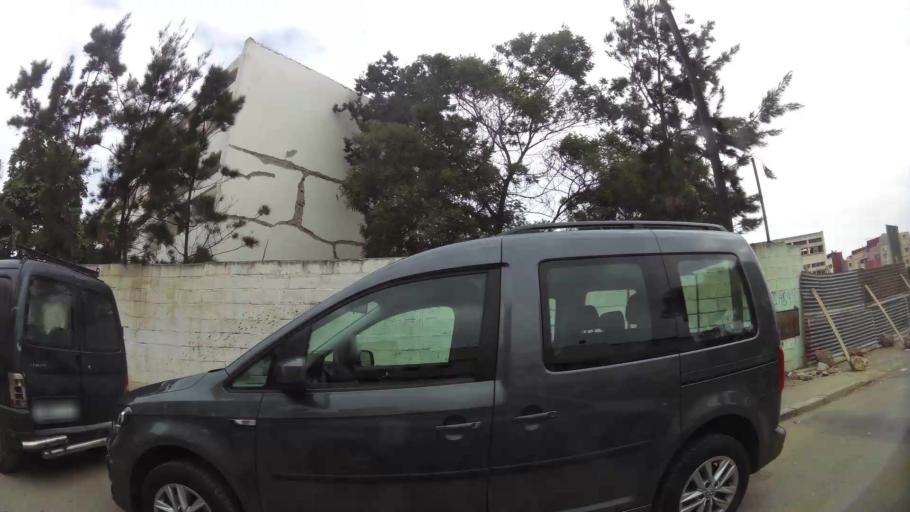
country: MA
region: Rabat-Sale-Zemmour-Zaer
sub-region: Rabat
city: Rabat
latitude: 33.9921
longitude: -6.8758
